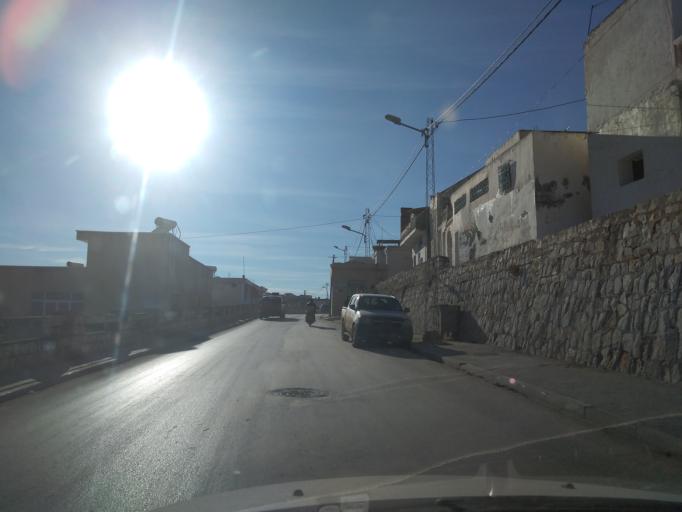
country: TN
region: Ariana
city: Qal'at al Andalus
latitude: 37.0615
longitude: 10.1163
